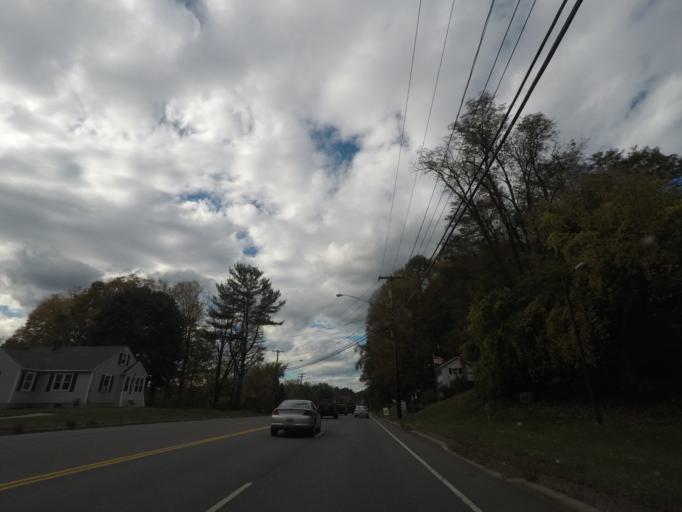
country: US
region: New York
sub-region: Albany County
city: Westmere
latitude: 42.7006
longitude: -73.9029
